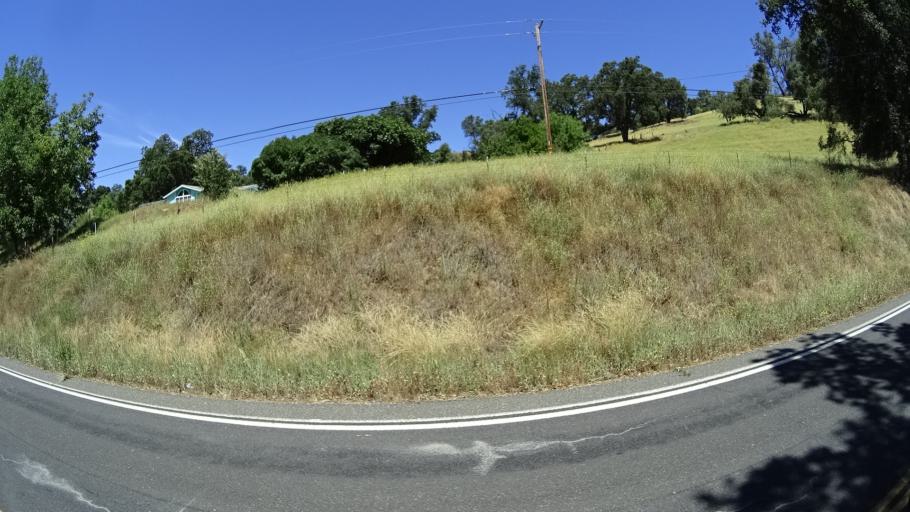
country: US
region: California
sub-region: Calaveras County
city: Angels Camp
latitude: 38.1113
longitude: -120.5078
